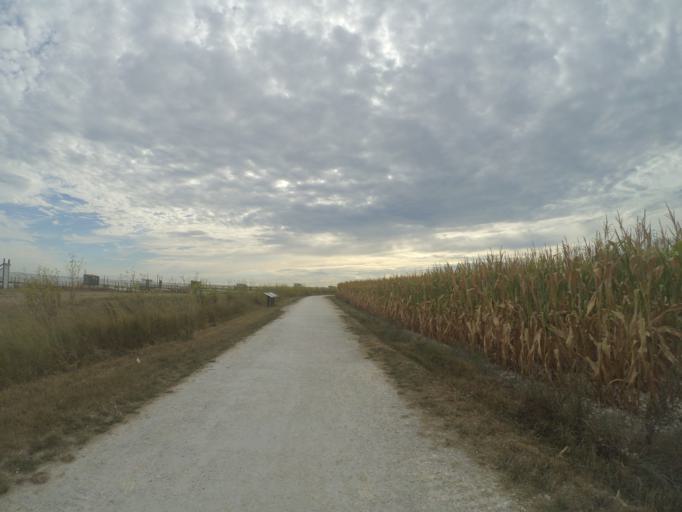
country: FR
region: Poitou-Charentes
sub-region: Departement de la Charente-Maritime
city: Meschers-sur-Gironde
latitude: 45.5514
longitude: -0.9217
